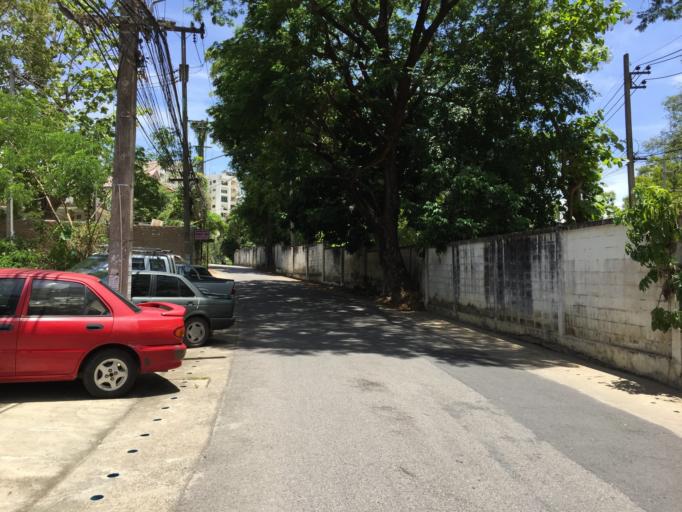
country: TH
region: Chiang Mai
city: Chiang Mai
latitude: 18.8021
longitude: 98.9572
